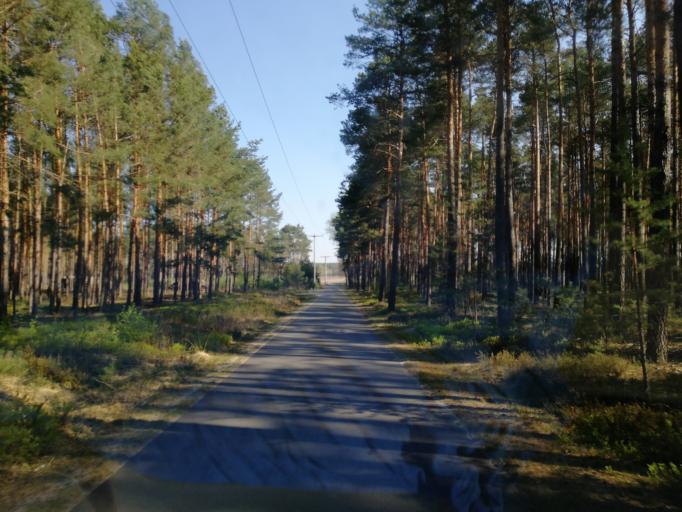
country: DE
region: Brandenburg
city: Bronkow
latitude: 51.6585
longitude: 13.8567
